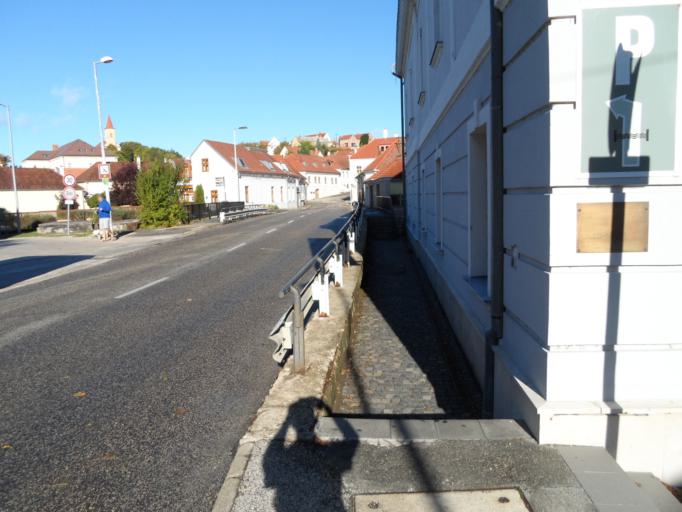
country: HU
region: Veszprem
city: Veszprem
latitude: 47.0972
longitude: 17.9011
